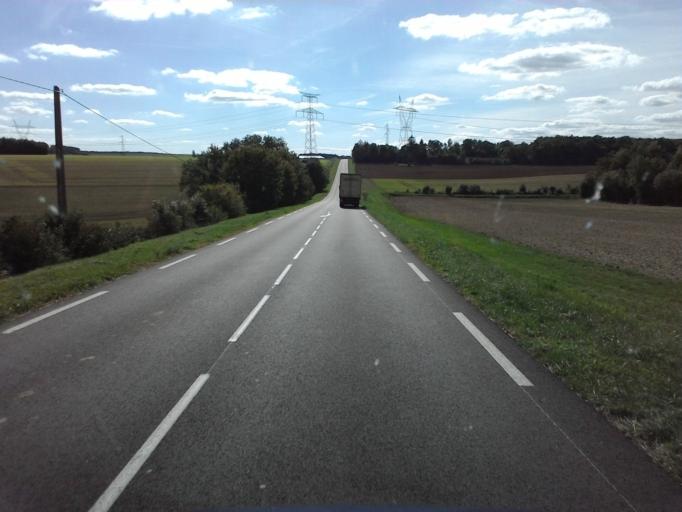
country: FR
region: Bourgogne
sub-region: Departement de la Cote-d'Or
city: Chatillon-sur-Seine
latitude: 47.7443
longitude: 4.4855
